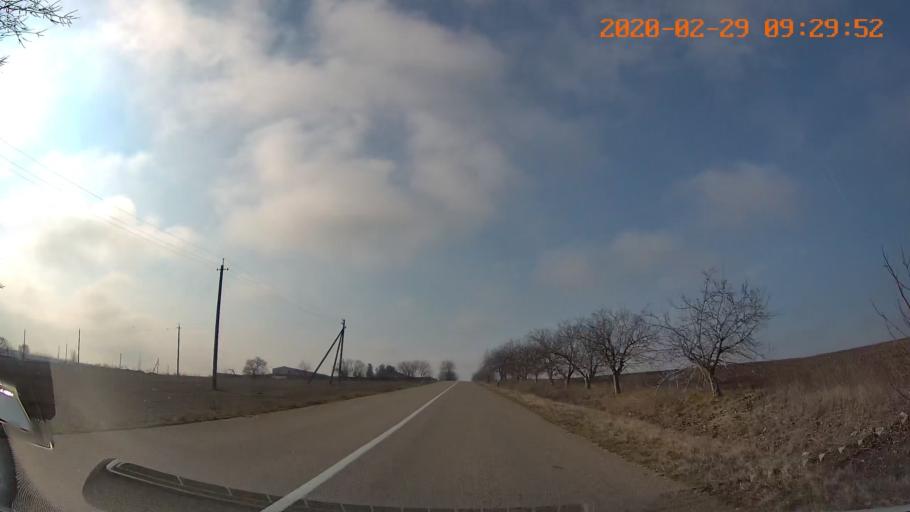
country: UA
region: Odessa
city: Lymanske
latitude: 46.6732
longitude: 29.9191
